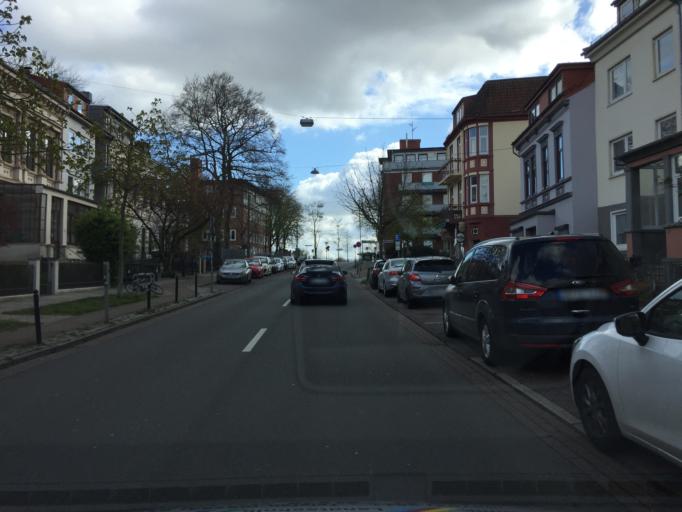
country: DE
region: Bremen
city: Bremen
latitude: 53.0701
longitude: 8.8242
